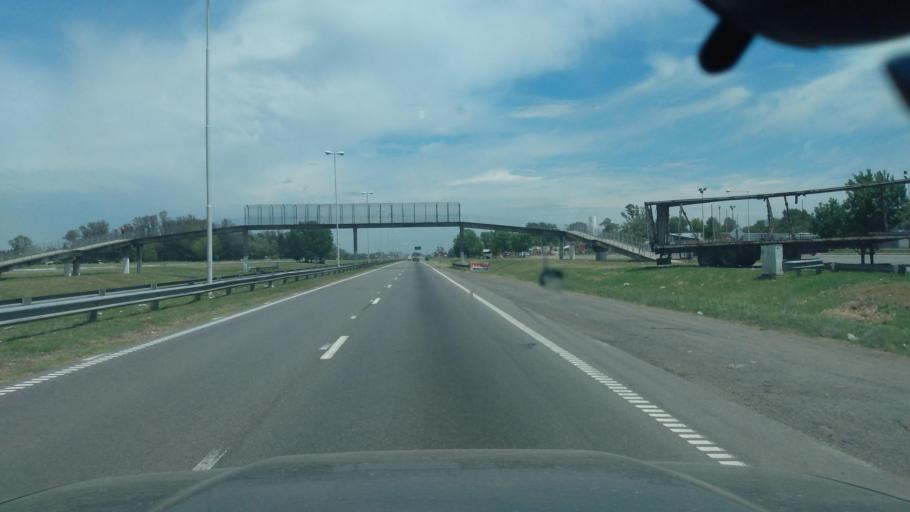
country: AR
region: Buenos Aires
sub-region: Partido de Lujan
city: Lujan
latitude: -34.5598
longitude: -59.0922
